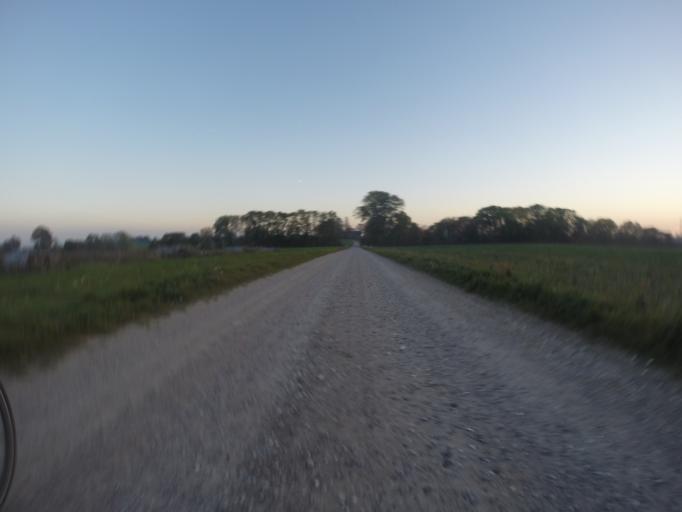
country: DK
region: Capital Region
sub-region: Hoje-Taastrup Kommune
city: Taastrup
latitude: 55.6774
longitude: 12.2938
